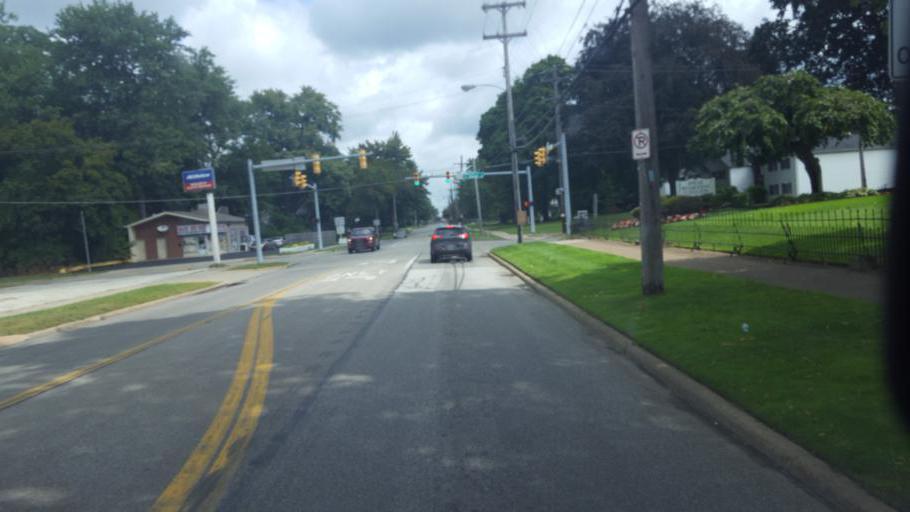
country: US
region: Ohio
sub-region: Lake County
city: Painesville
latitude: 41.7148
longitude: -81.2575
